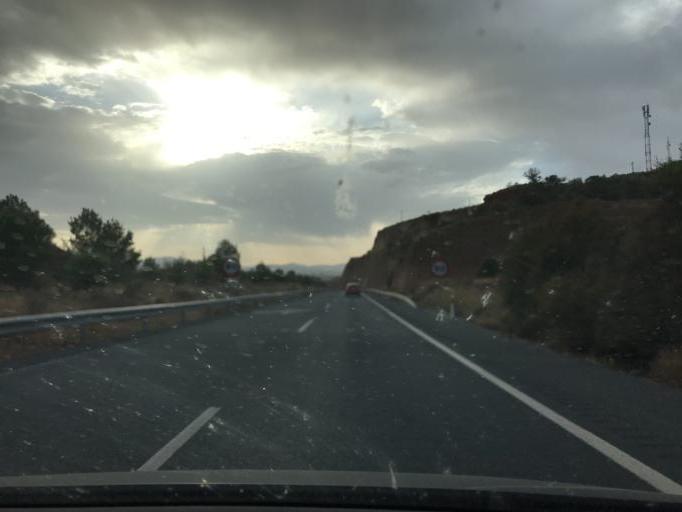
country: ES
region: Andalusia
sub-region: Provincia de Granada
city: Guadix
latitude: 37.3217
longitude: -3.1161
